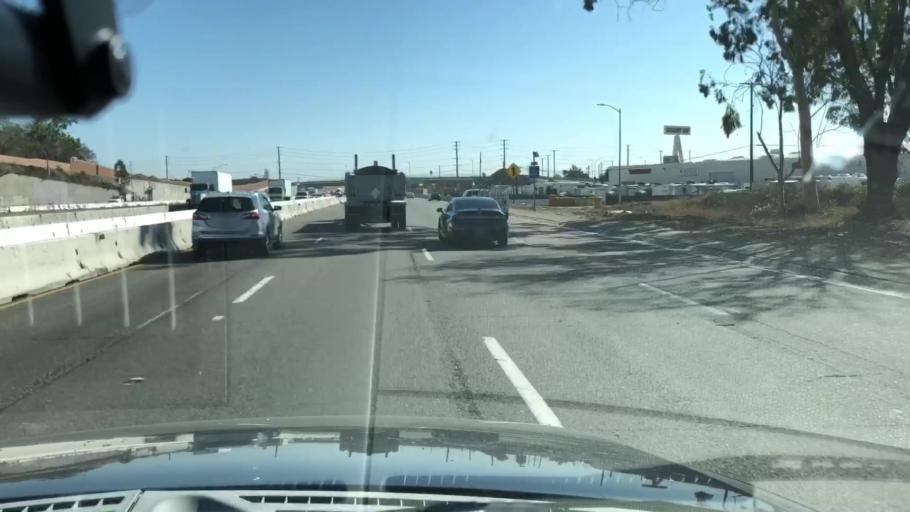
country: US
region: California
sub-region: Los Angeles County
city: Santa Fe Springs
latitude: 33.9393
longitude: -118.0954
